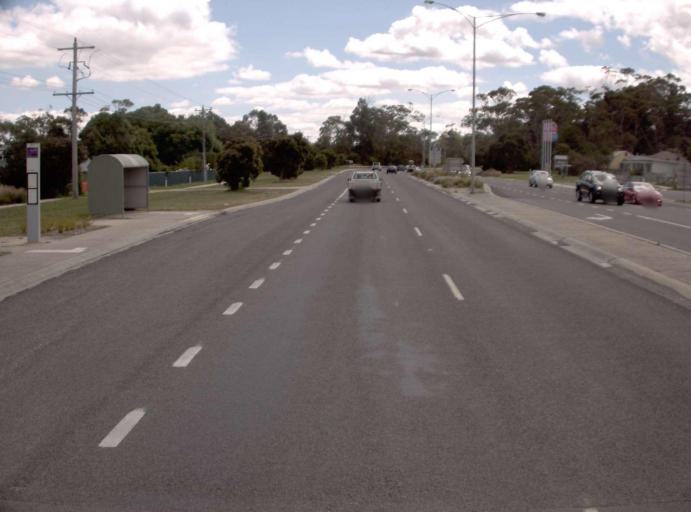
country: AU
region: Victoria
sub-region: Bass Coast
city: North Wonthaggi
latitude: -38.4073
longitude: 145.5303
